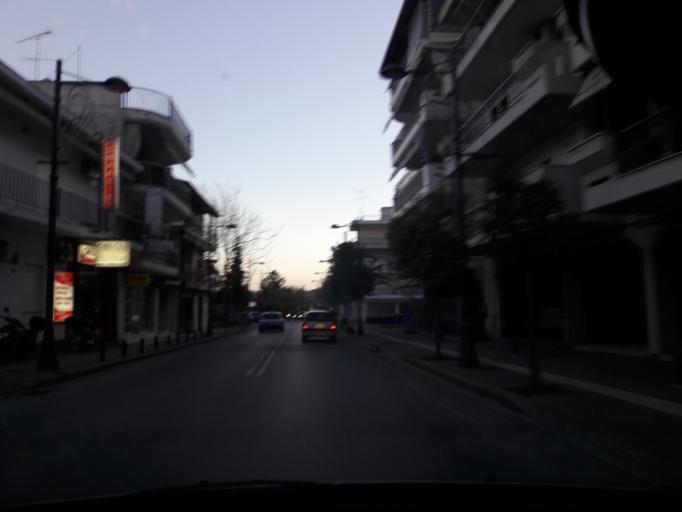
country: GR
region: Central Macedonia
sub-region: Nomos Thessalonikis
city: Stavroupoli
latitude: 40.6674
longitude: 22.9325
